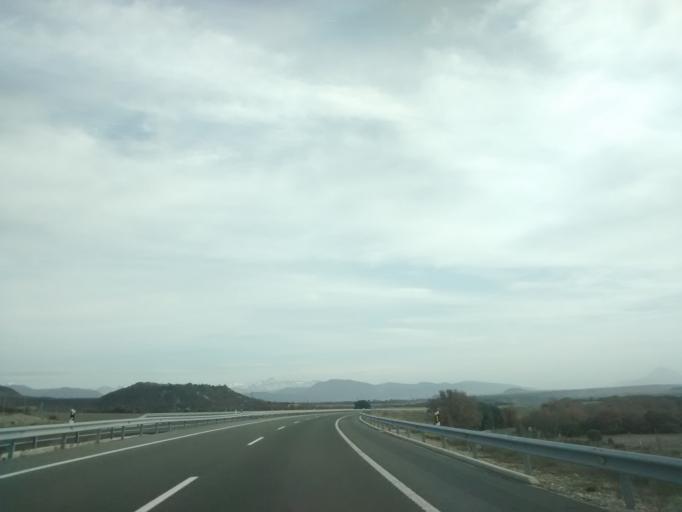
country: ES
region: Aragon
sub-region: Provincia de Zaragoza
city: Mianos
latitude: 42.6099
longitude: -0.9662
